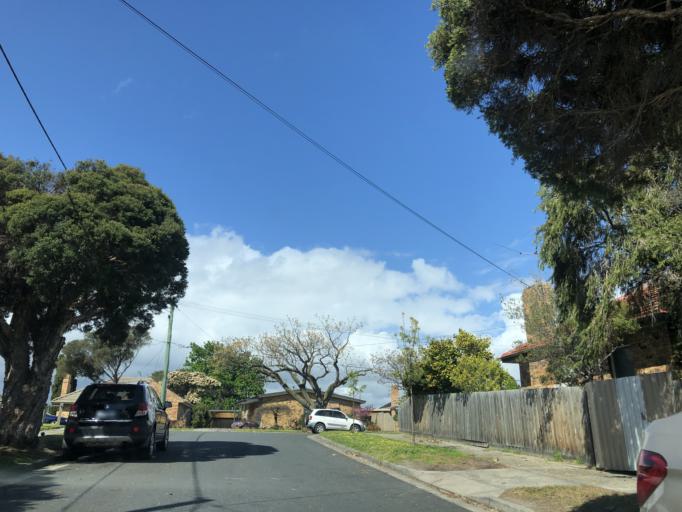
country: AU
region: Victoria
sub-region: Kingston
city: Clayton South
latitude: -37.9279
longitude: 145.1061
